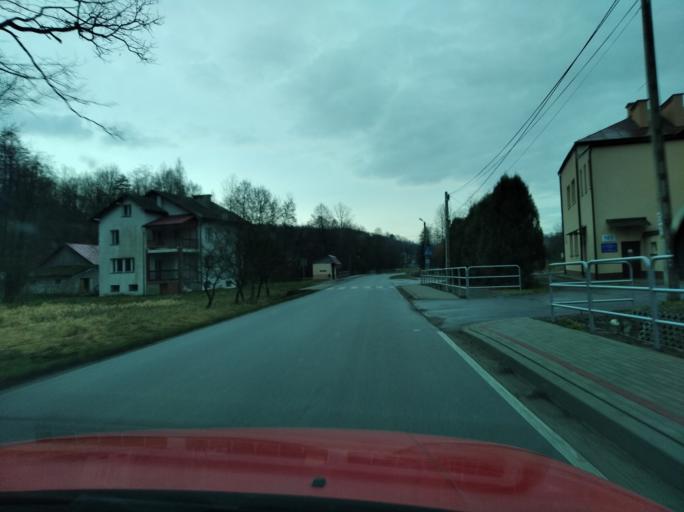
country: PL
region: Subcarpathian Voivodeship
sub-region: Powiat strzyzowski
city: Gwoznica Gorna
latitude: 49.8375
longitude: 21.9877
